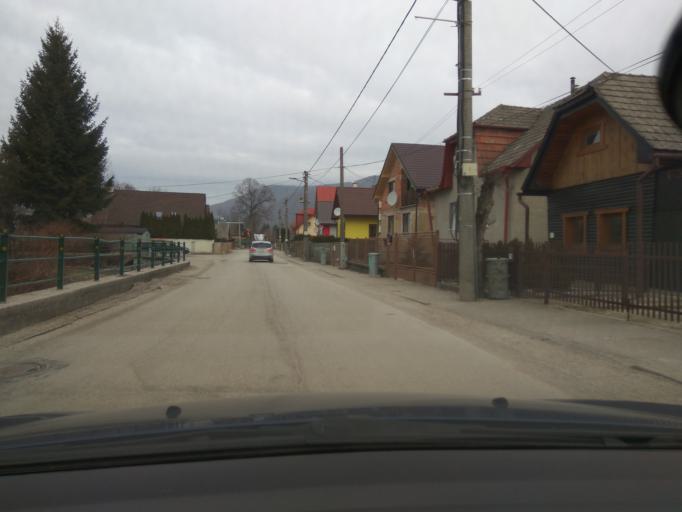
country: SK
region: Zilinsky
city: Rajec
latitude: 49.1149
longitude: 18.6776
